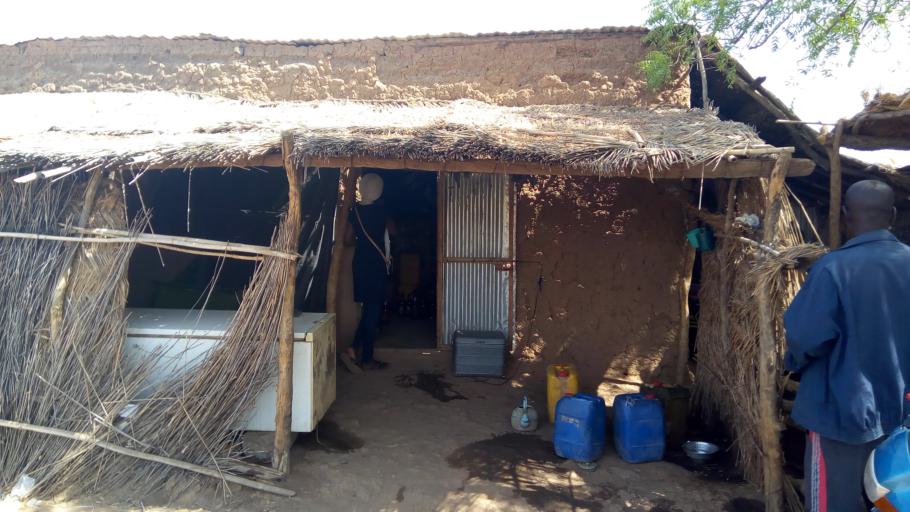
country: ML
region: Kayes
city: Yelimane
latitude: 14.6425
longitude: -10.7001
